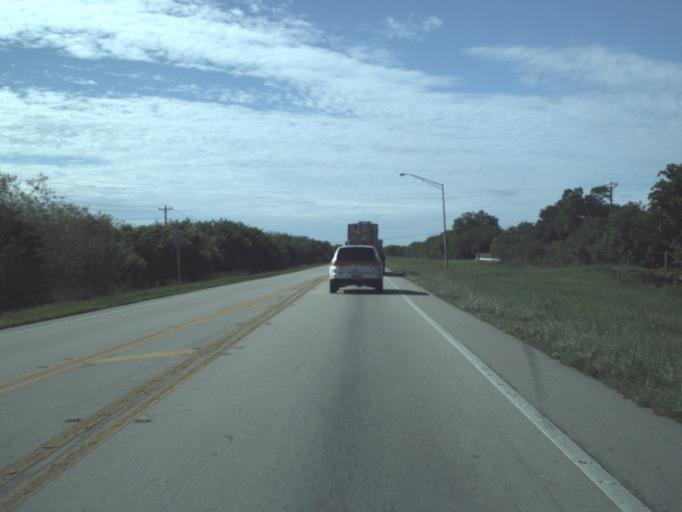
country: US
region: Florida
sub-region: Collier County
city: Immokalee
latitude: 26.4842
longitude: -81.4347
